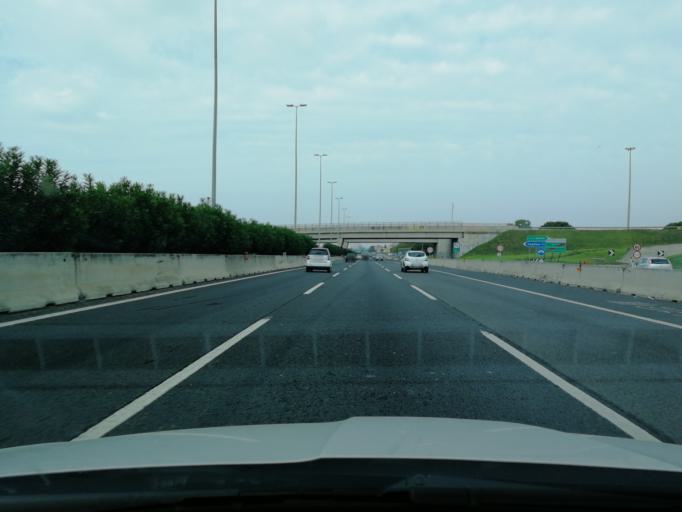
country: IT
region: Latium
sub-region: Citta metropolitana di Roma Capitale
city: Ciampino
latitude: 41.8516
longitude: 12.5970
